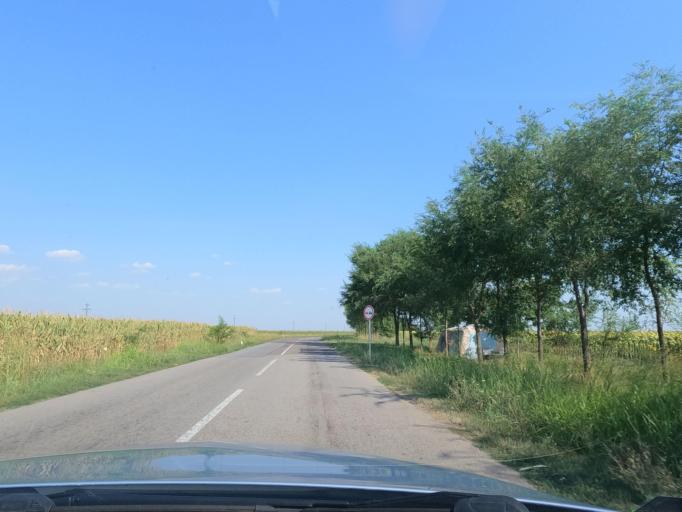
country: RS
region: Autonomna Pokrajina Vojvodina
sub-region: Juznobacki Okrug
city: Becej
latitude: 45.6512
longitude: 19.9741
